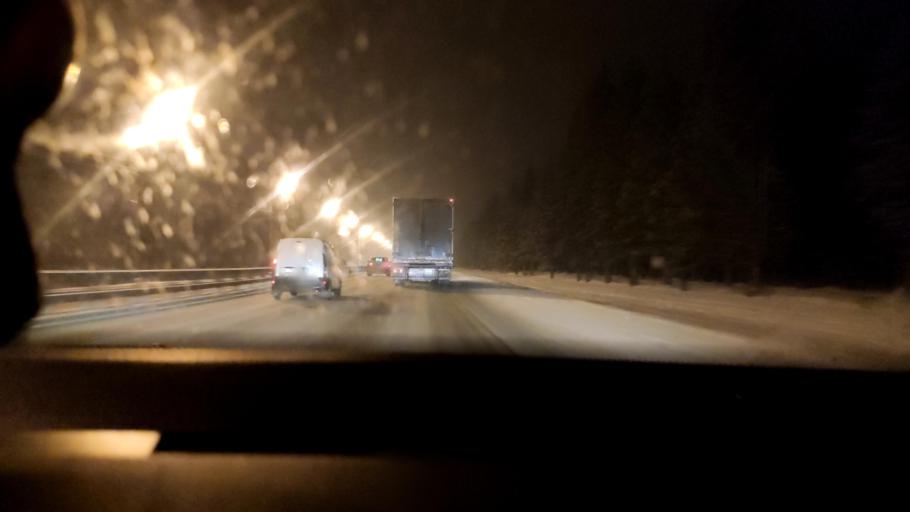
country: RU
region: Moskovskaya
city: Selyatino
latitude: 55.4806
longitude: 36.9430
